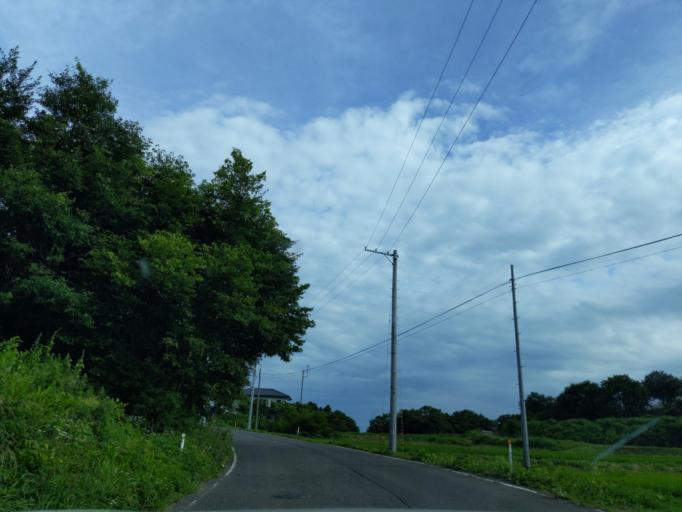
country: JP
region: Fukushima
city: Koriyama
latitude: 37.3428
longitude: 140.3068
